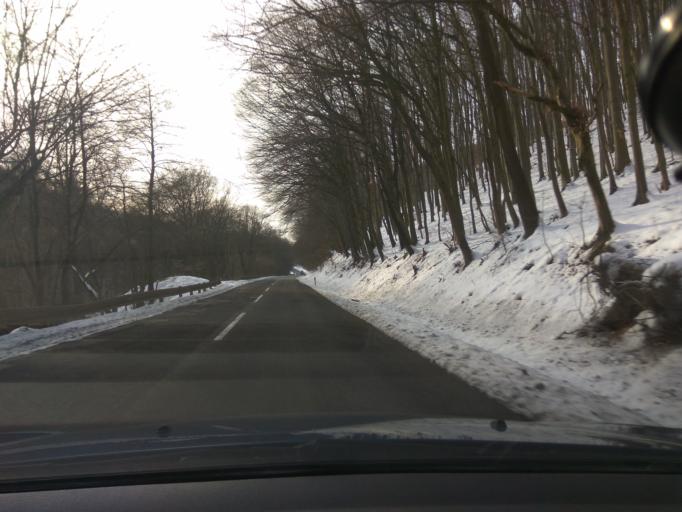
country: SK
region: Nitriansky
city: Novaky
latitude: 48.5847
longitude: 18.5216
